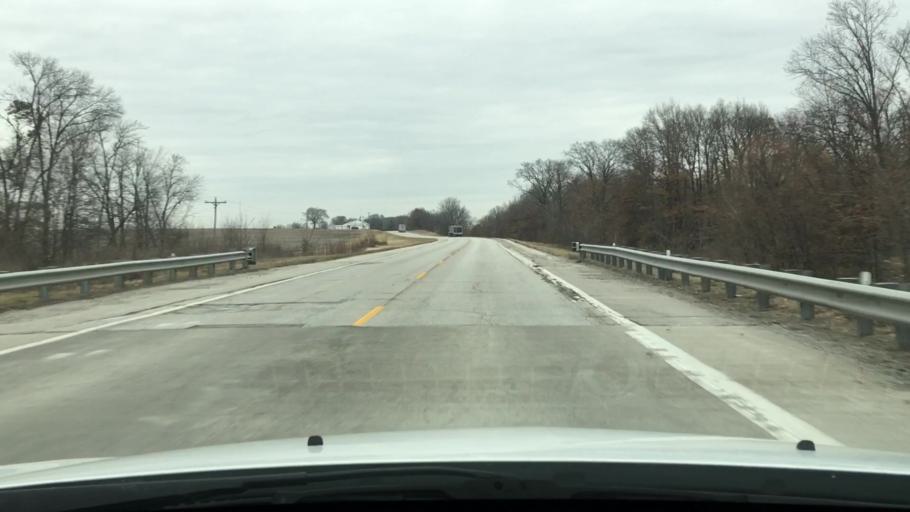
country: US
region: Missouri
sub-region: Montgomery County
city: Wellsville
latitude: 39.2004
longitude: -91.6463
